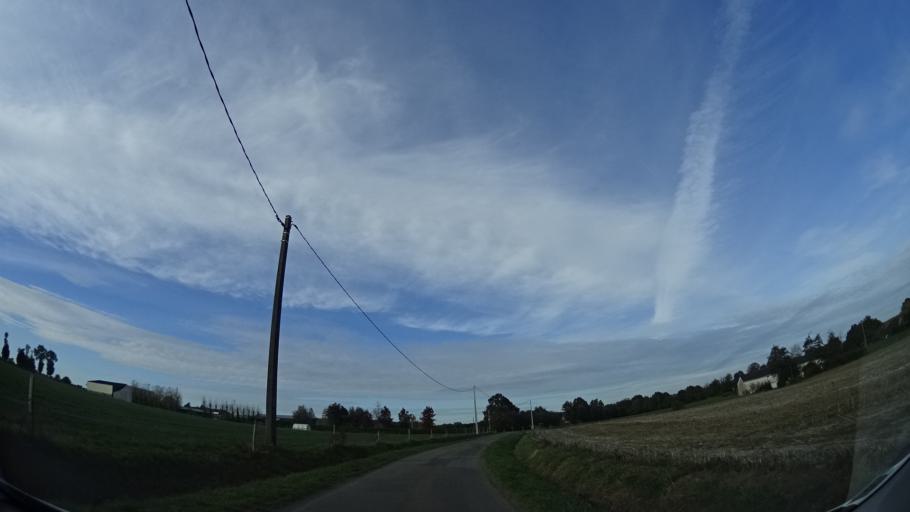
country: FR
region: Brittany
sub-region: Departement d'Ille-et-Vilaine
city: Geveze
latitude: 48.2394
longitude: -1.8293
